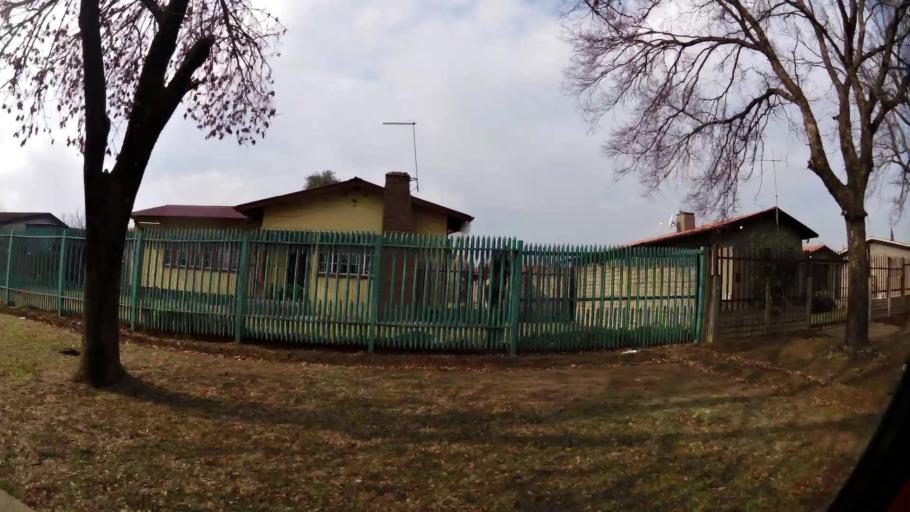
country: ZA
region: Gauteng
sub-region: Sedibeng District Municipality
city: Vanderbijlpark
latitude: -26.6882
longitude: 27.8394
